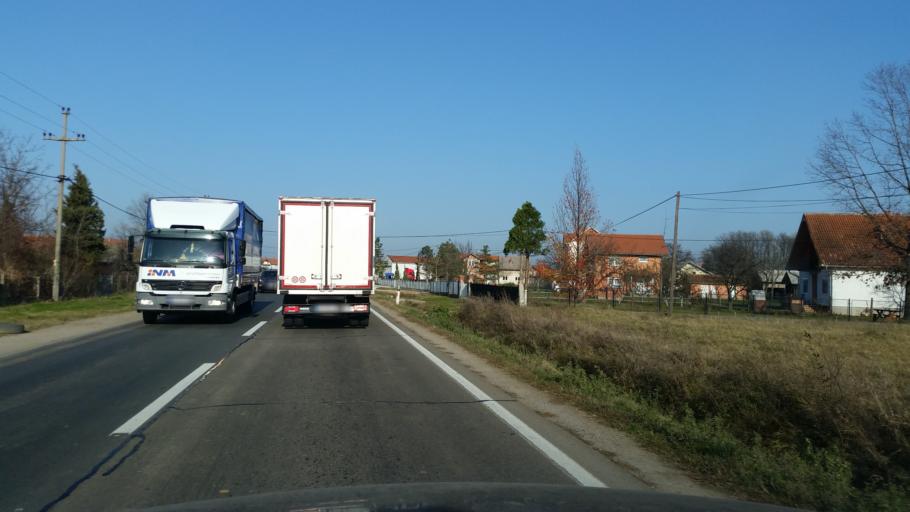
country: RS
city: Stepojevac
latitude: 44.5320
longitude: 20.2975
